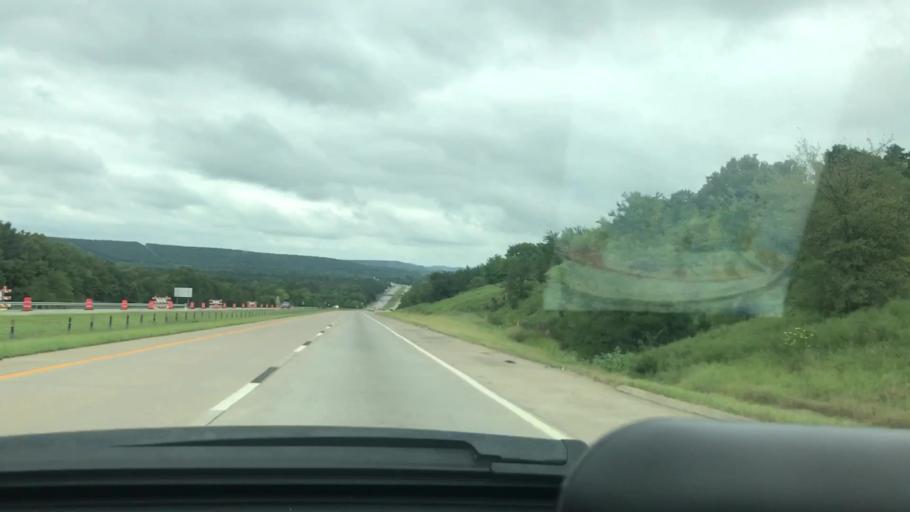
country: US
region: Oklahoma
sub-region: Pittsburg County
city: Krebs
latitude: 34.9910
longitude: -95.7216
